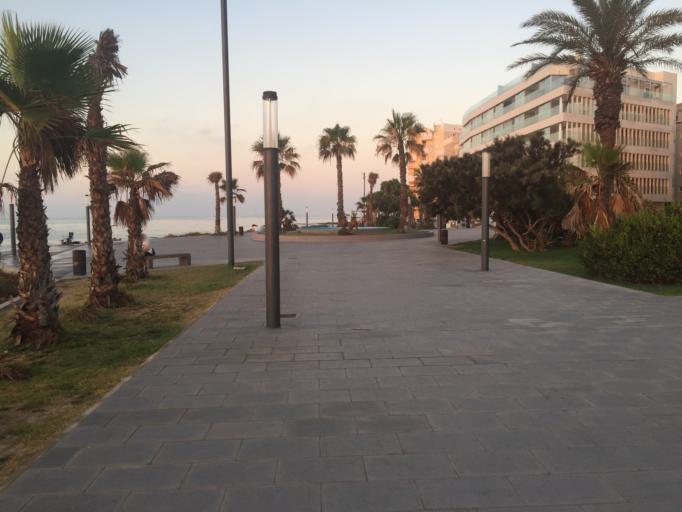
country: ES
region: Valencia
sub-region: Provincia de Alicante
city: Torrevieja
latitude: 37.9785
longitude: -0.6643
